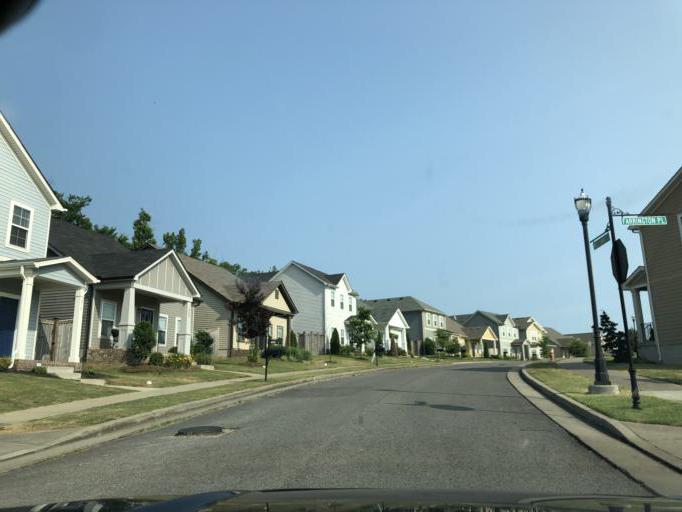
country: US
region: Tennessee
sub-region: Rutherford County
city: La Vergne
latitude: 36.0484
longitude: -86.6429
